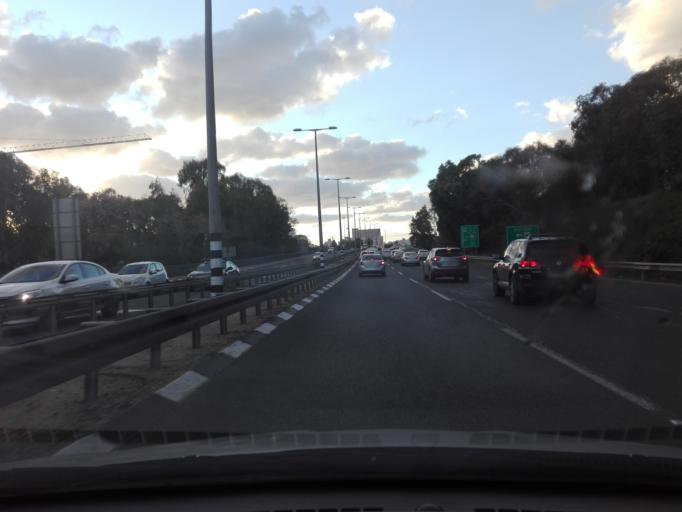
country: IL
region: Central District
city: Bet Yizhaq
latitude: 32.3244
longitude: 34.8735
